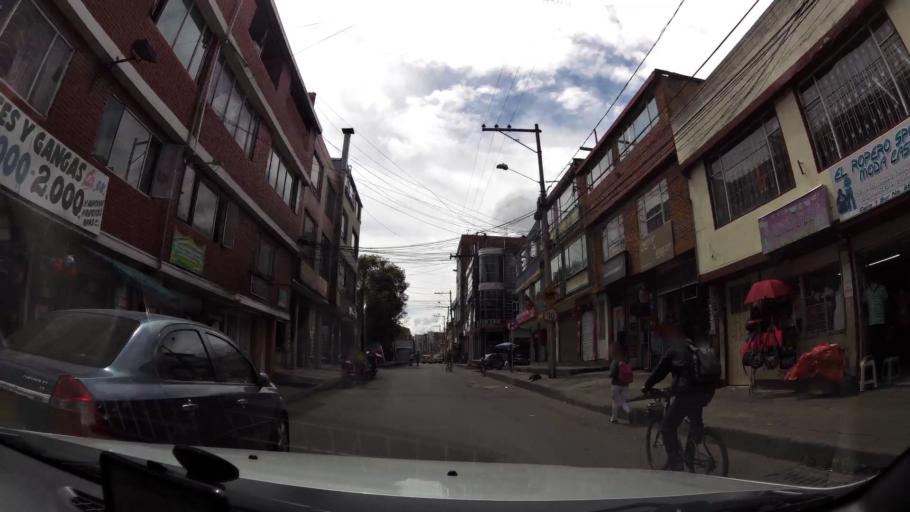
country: CO
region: Bogota D.C.
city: Bogota
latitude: 4.6208
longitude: -74.1270
